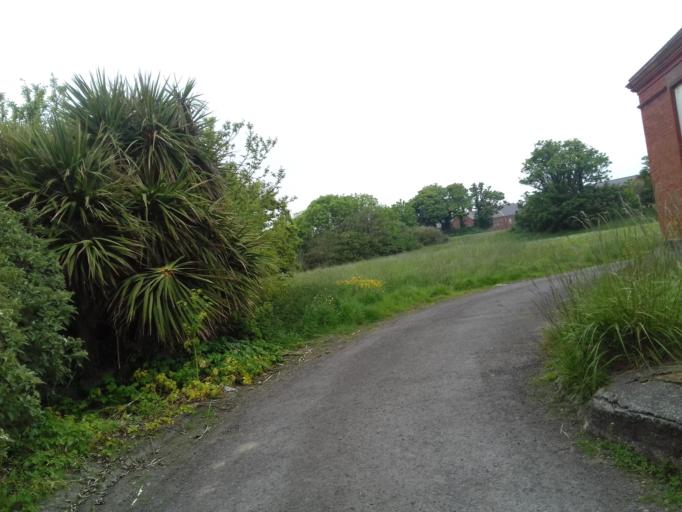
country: IE
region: Leinster
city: Portraine
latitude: 53.4843
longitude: -6.1101
